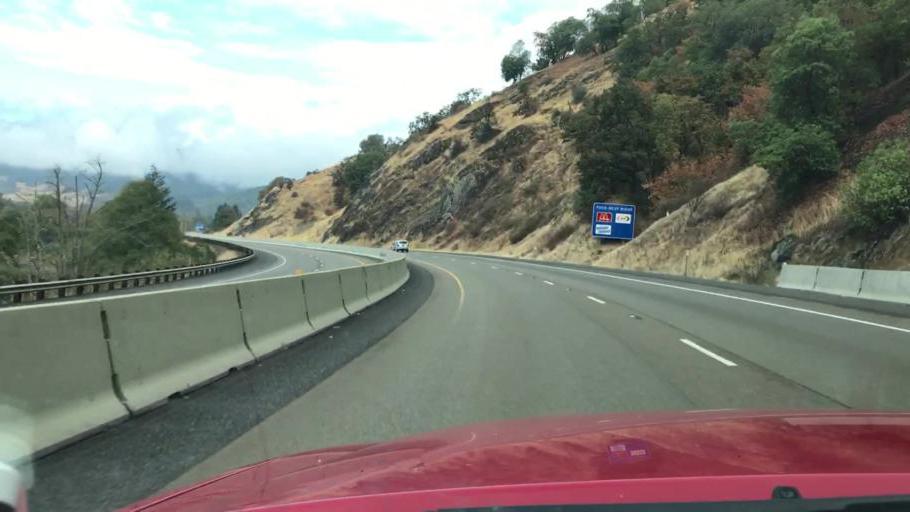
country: US
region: Oregon
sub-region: Douglas County
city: Tri-City
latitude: 42.9616
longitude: -123.3259
